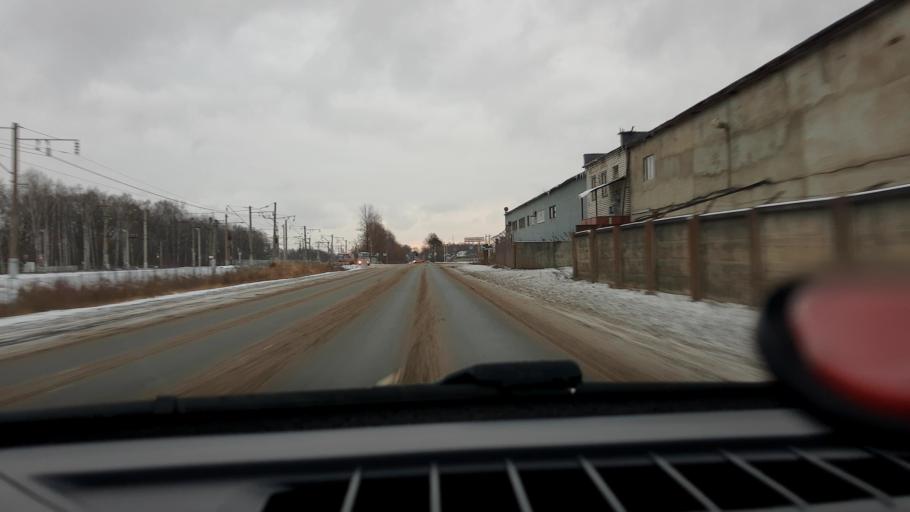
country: RU
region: Nizjnij Novgorod
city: Gorbatovka
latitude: 56.2627
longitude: 43.7279
